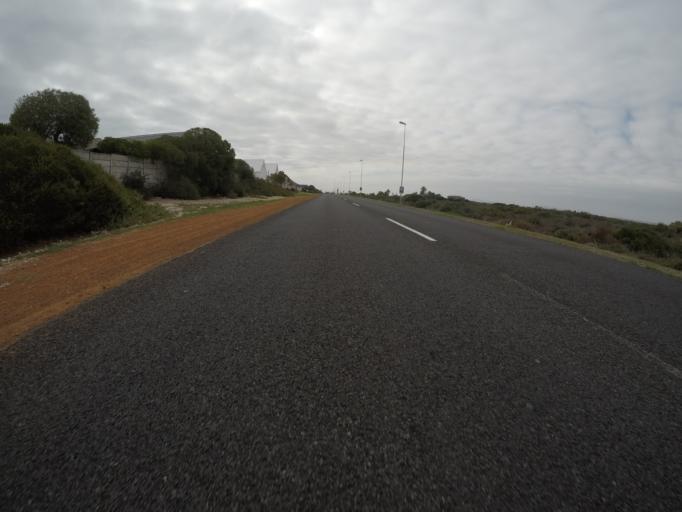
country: ZA
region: Western Cape
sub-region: City of Cape Town
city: Atlantis
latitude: -33.7040
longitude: 18.4461
